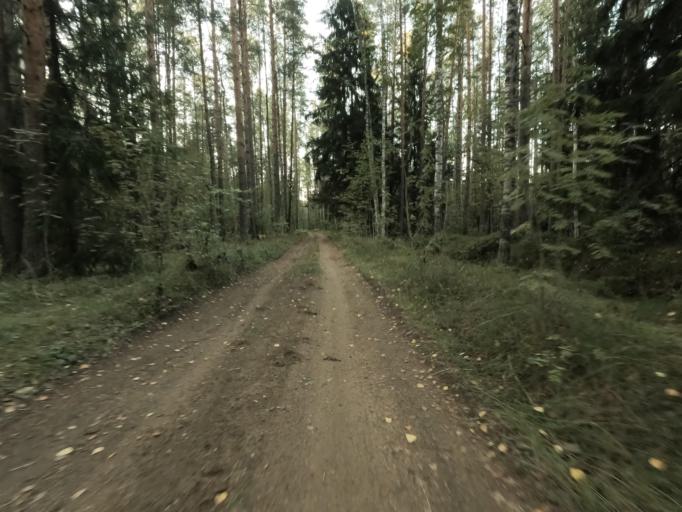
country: RU
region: Leningrad
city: Otradnoye
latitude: 59.8342
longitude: 30.8087
